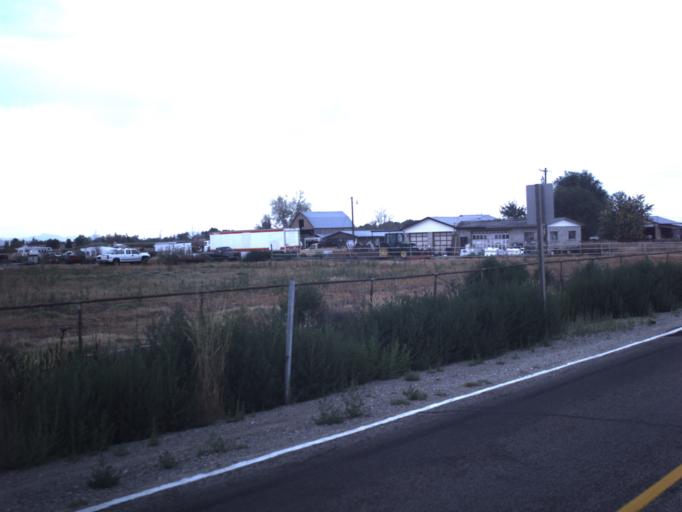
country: US
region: Utah
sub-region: Weber County
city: Hooper
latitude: 41.1639
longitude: -112.0942
